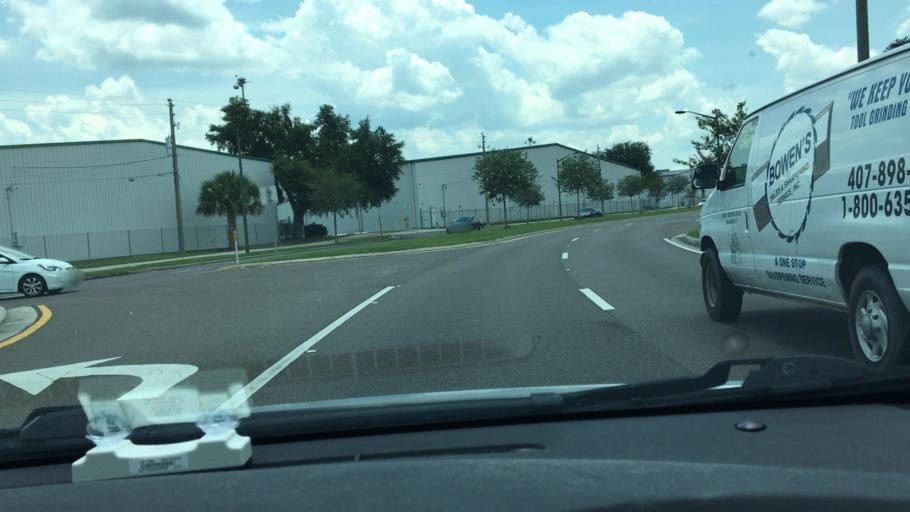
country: US
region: Florida
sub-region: Orange County
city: Orlando
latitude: 28.5455
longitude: -81.3440
